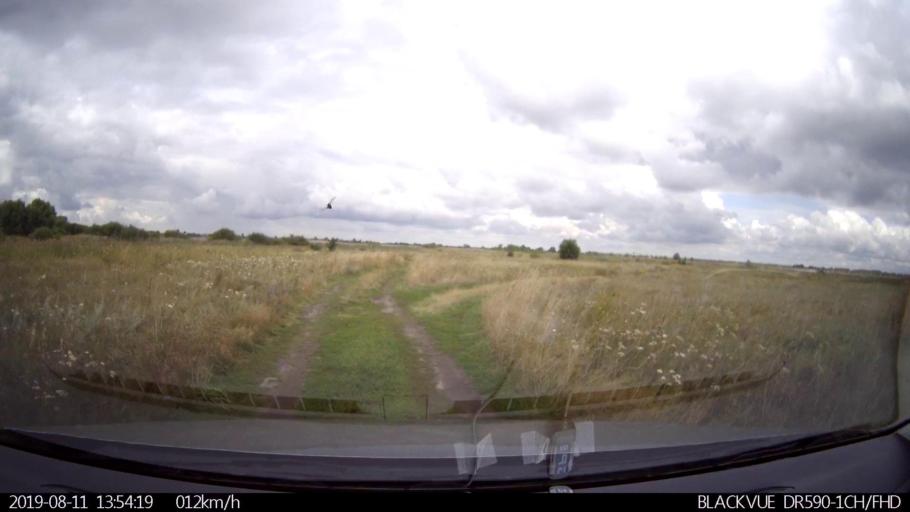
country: RU
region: Ulyanovsk
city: Ignatovka
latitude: 53.8443
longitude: 47.5864
